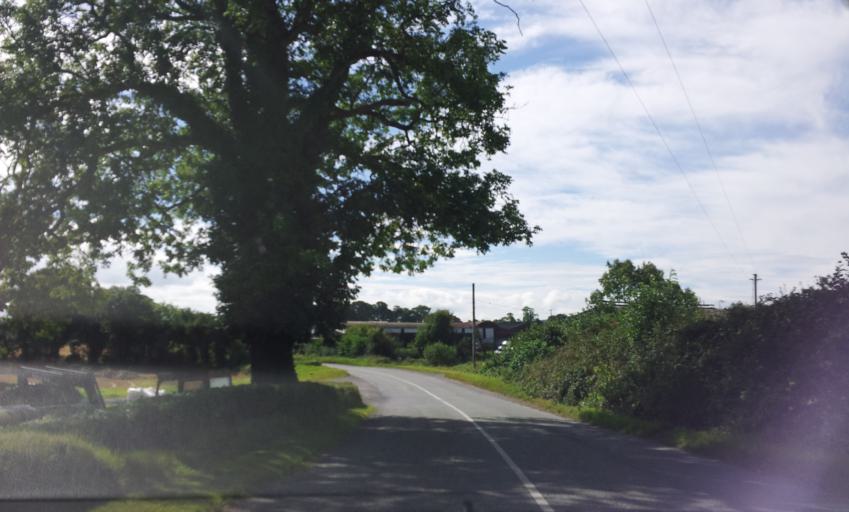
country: IE
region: Leinster
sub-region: Laois
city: Stradbally
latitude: 52.9813
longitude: -7.2152
